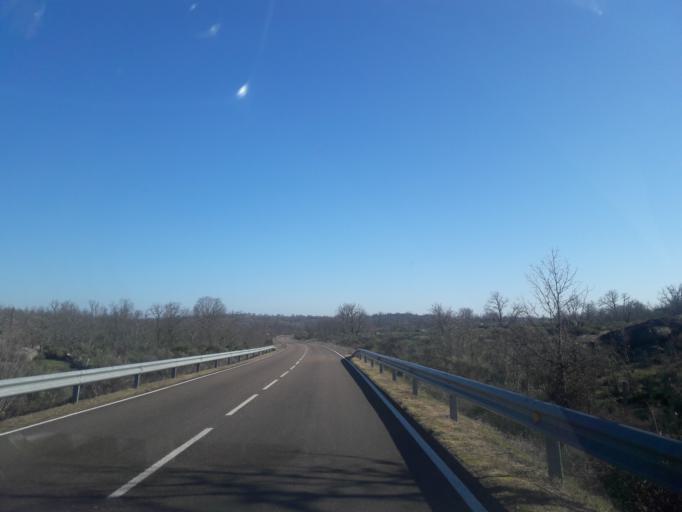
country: ES
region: Castille and Leon
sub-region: Provincia de Salamanca
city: Cabeza del Caballo
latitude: 41.0880
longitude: -6.5586
